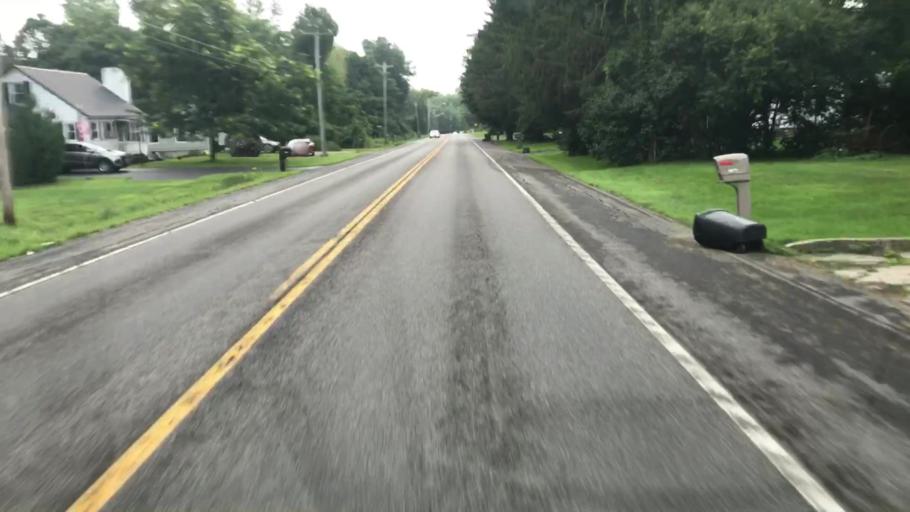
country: US
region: New York
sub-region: Onondaga County
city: Liverpool
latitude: 43.1811
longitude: -76.1995
